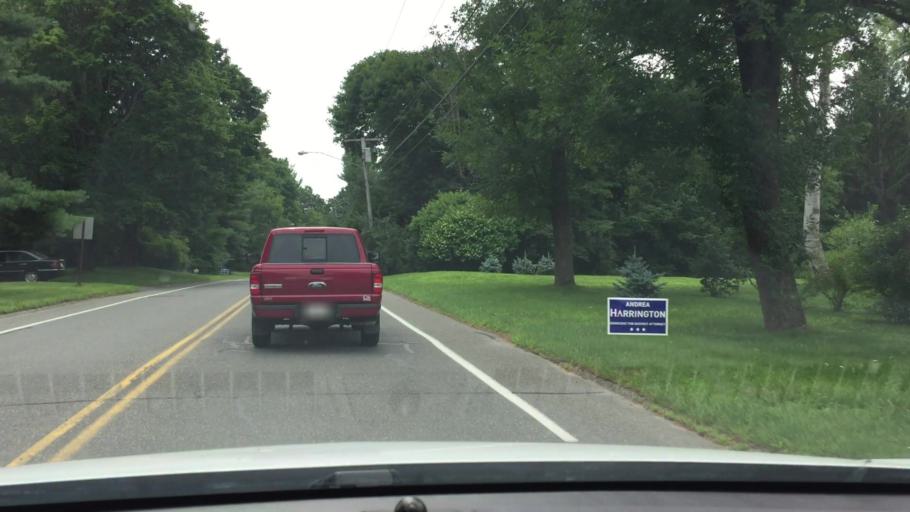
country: US
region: Massachusetts
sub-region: Berkshire County
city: Pittsfield
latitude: 42.4322
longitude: -73.2379
